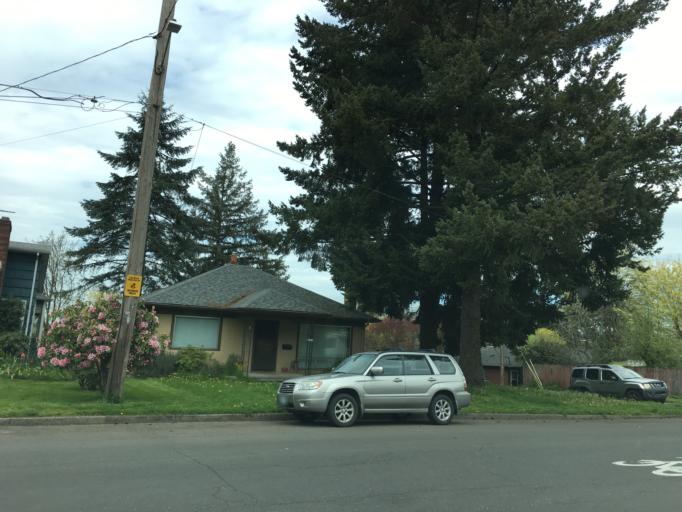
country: US
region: Oregon
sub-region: Multnomah County
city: Lents
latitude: 45.5241
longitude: -122.5961
